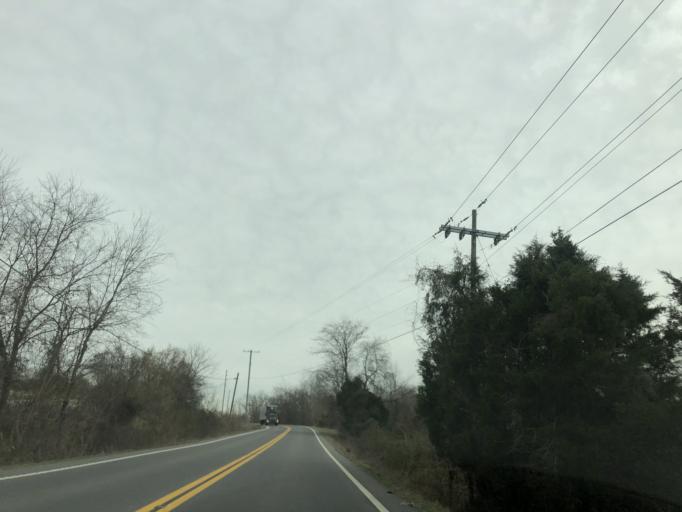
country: US
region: Tennessee
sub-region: Robertson County
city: Greenbrier
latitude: 36.4830
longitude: -86.7901
